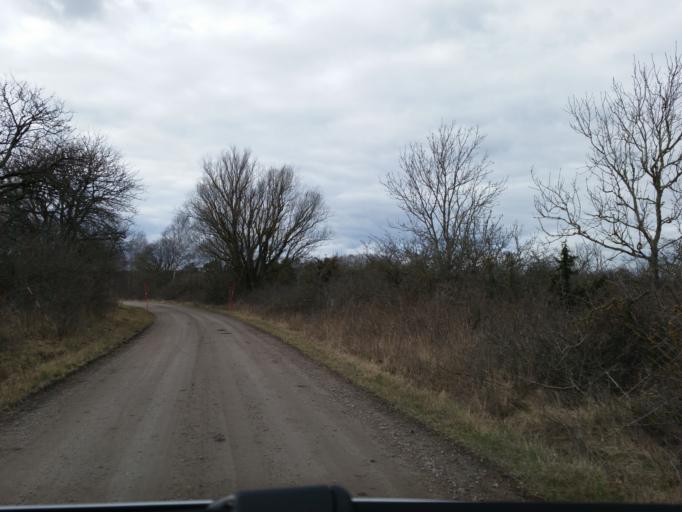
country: SE
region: Kalmar
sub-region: Morbylanga Kommun
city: Sodra Sandby
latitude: 56.6614
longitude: 16.6950
